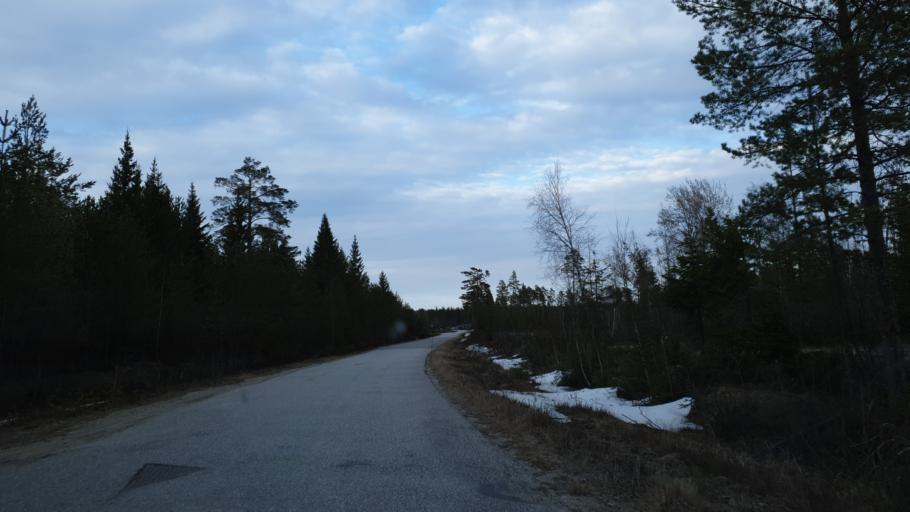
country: SE
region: Vaesternorrland
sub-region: Sundsvalls Kommun
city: Njurundabommen
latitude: 62.0301
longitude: 17.4071
